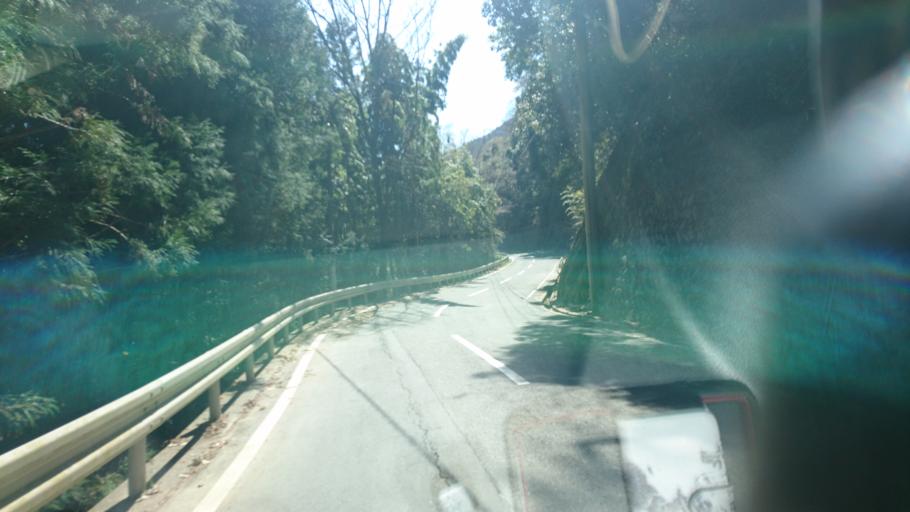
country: JP
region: Shizuoka
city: Fujinomiya
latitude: 35.3588
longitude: 138.4409
